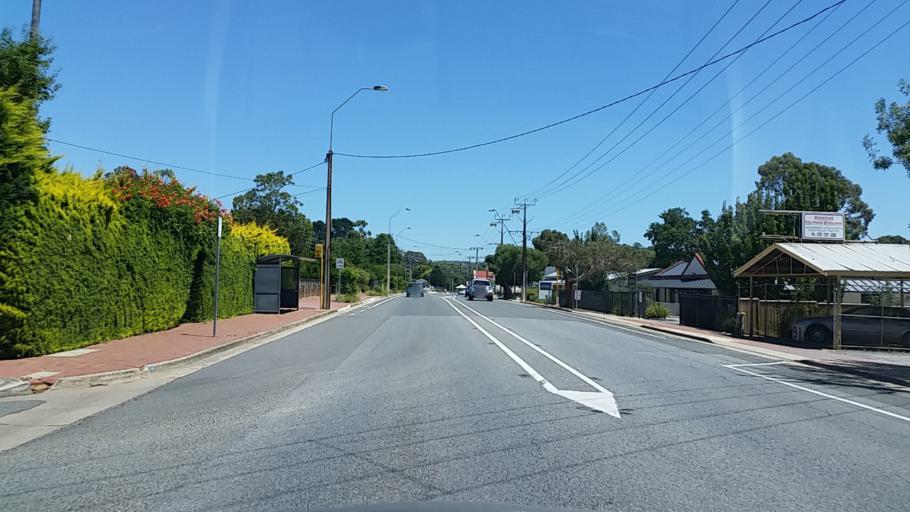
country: AU
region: South Australia
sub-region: Mount Barker
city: Little Hampton
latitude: -35.0478
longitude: 138.8679
